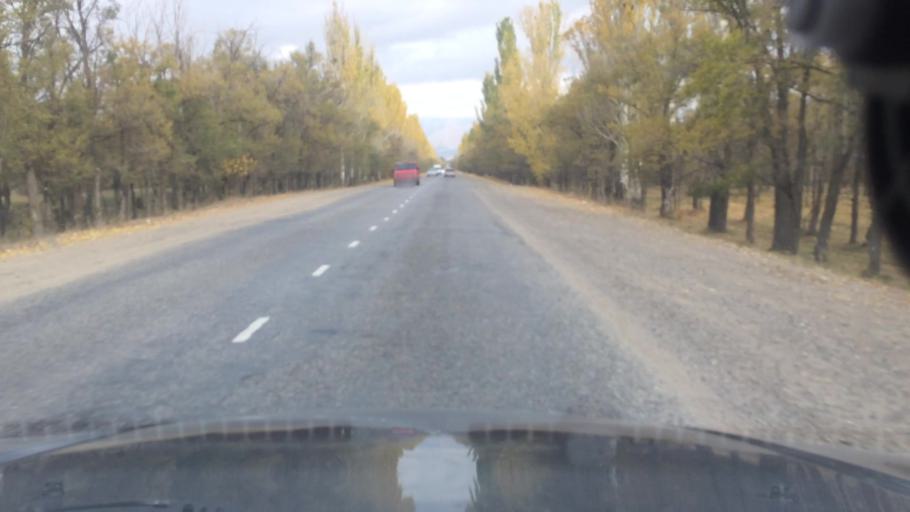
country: KG
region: Ysyk-Koel
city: Tyup
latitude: 42.6341
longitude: 78.3595
